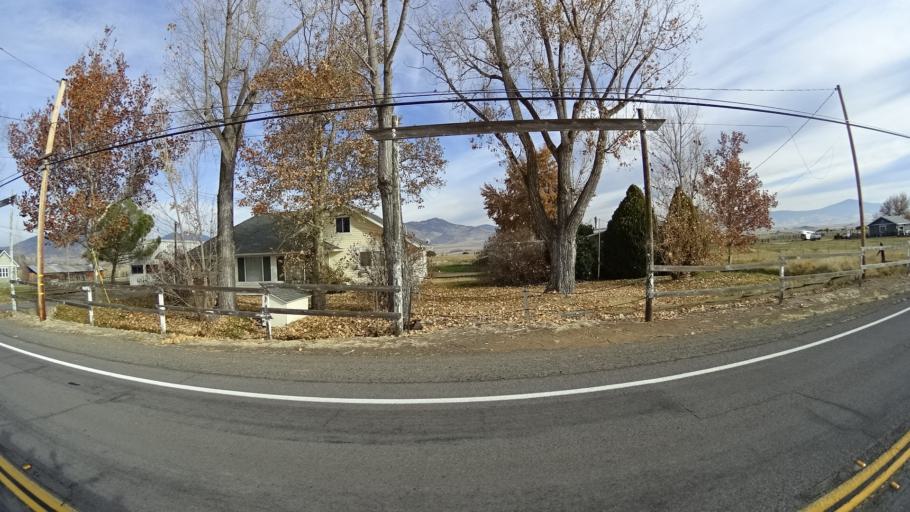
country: US
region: California
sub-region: Siskiyou County
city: Montague
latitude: 41.7305
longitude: -122.5772
